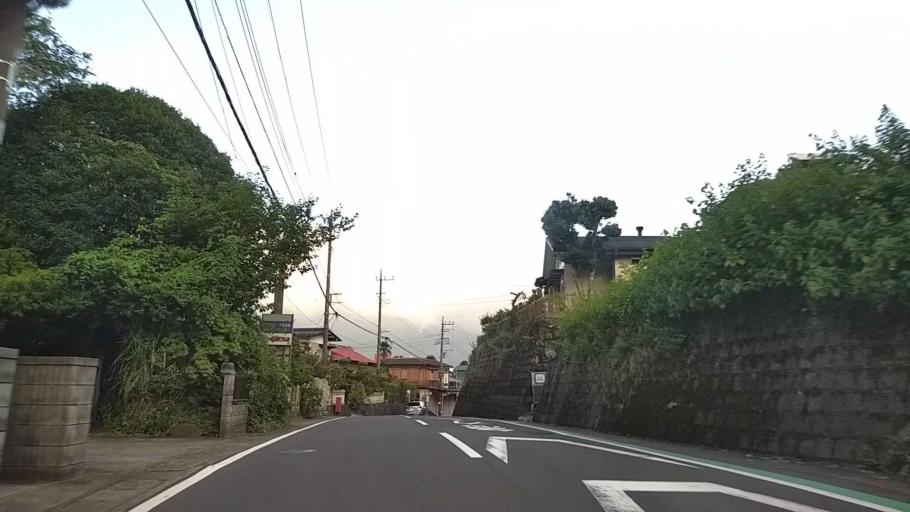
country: JP
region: Kanagawa
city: Atsugi
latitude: 35.4856
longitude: 139.2728
